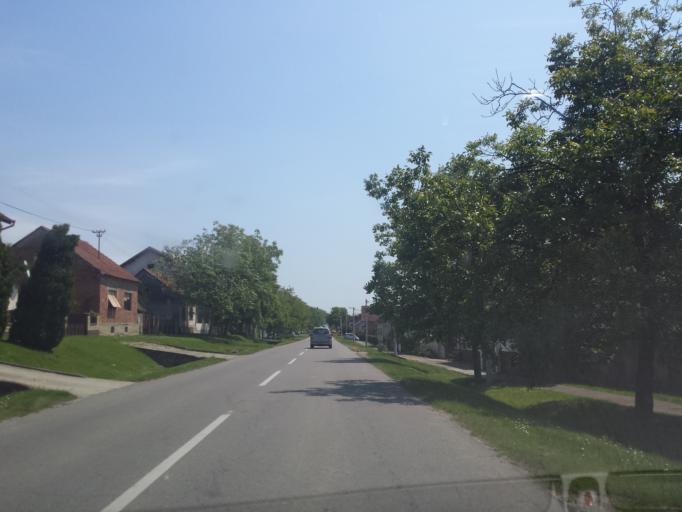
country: HR
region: Brodsko-Posavska
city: Oriovac
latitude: 45.1687
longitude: 17.7402
